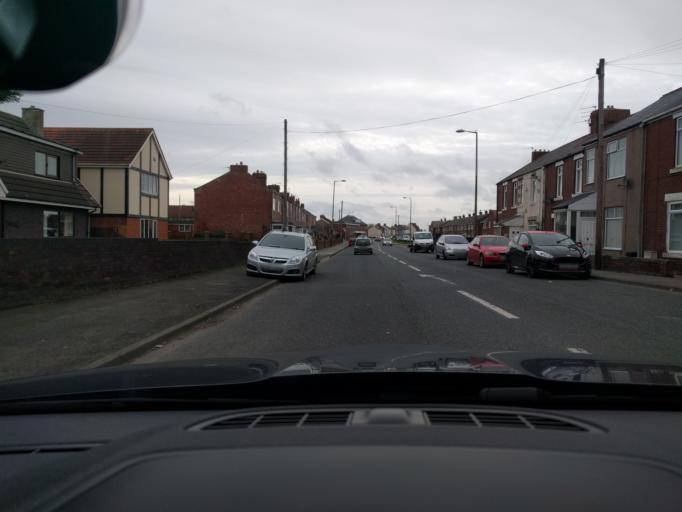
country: GB
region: England
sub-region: Northumberland
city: Ashington
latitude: 55.1607
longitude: -1.5975
